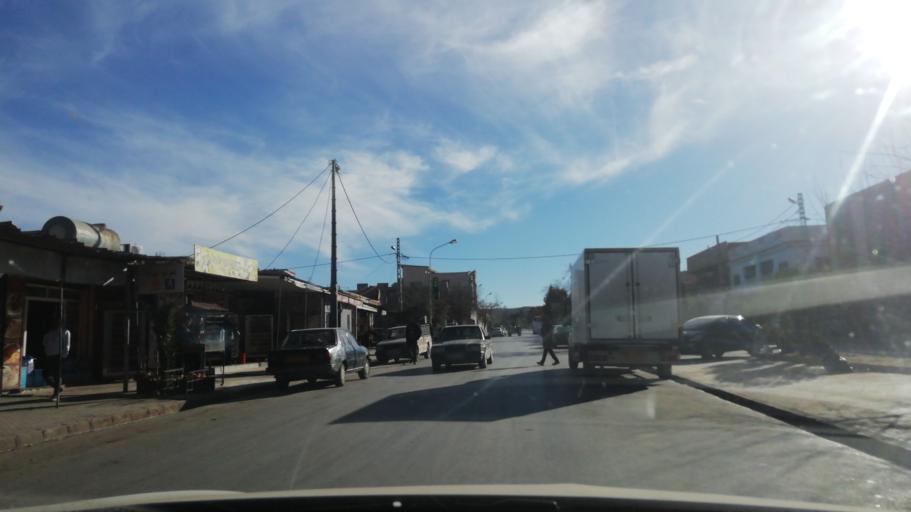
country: DZ
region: Tlemcen
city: Sebdou
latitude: 34.6309
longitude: -1.3333
